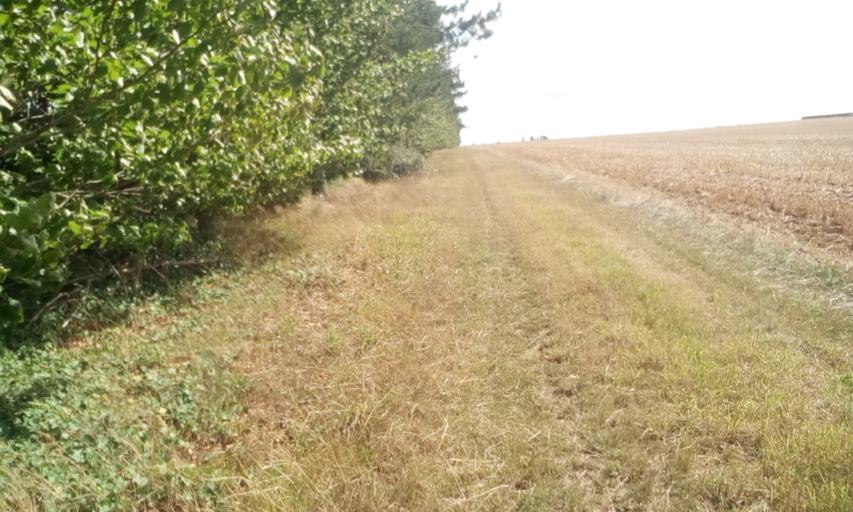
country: FR
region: Lower Normandy
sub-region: Departement du Calvados
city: Saint-Sylvain
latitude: 49.0806
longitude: -0.1981
